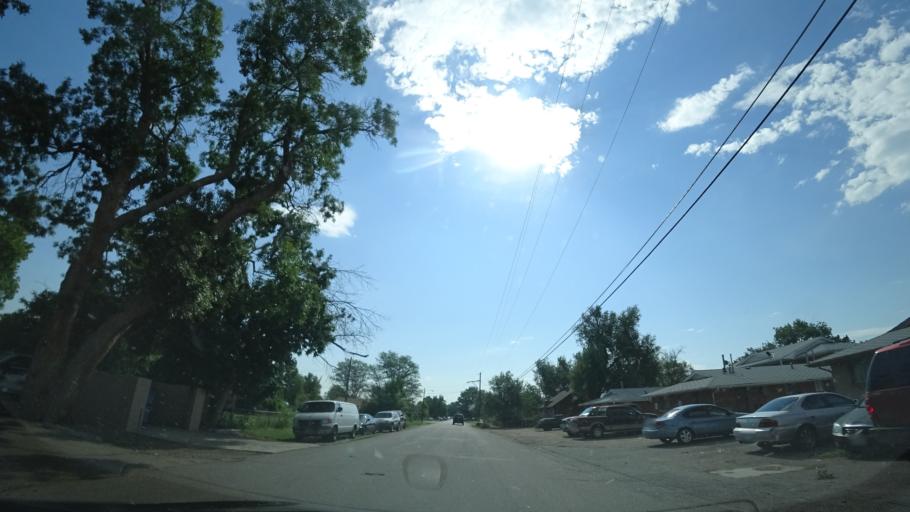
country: US
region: Colorado
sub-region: Jefferson County
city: Lakewood
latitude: 39.7231
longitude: -105.0575
